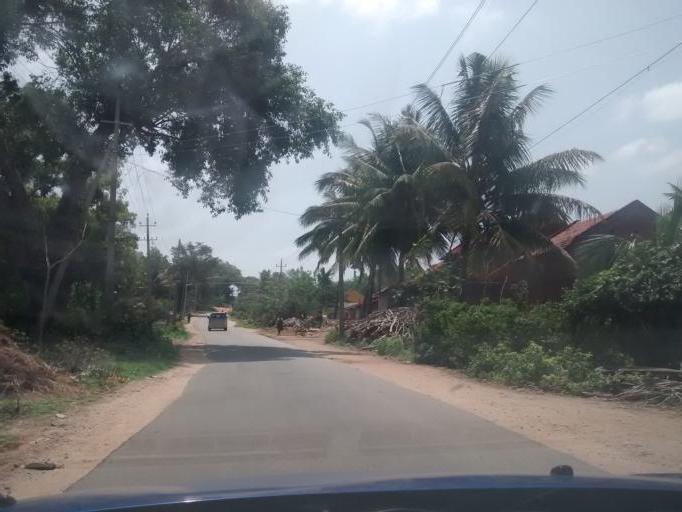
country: IN
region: Karnataka
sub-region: Mandya
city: Krishnarajpet
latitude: 12.5761
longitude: 76.3163
